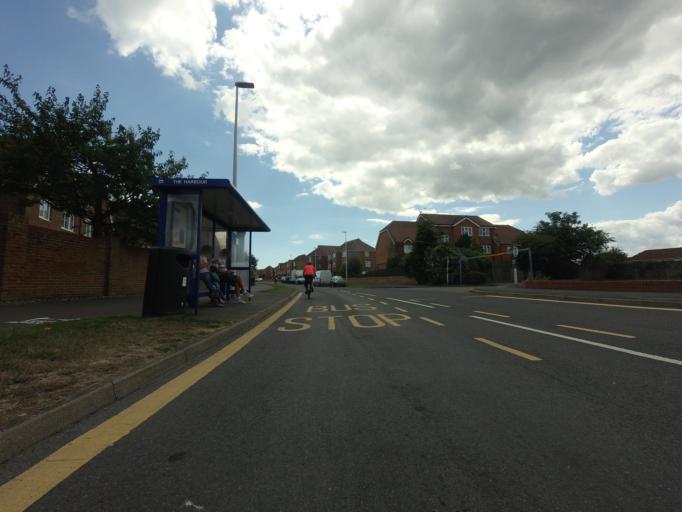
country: GB
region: England
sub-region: East Sussex
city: Pevensey
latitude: 50.7932
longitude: 0.3224
